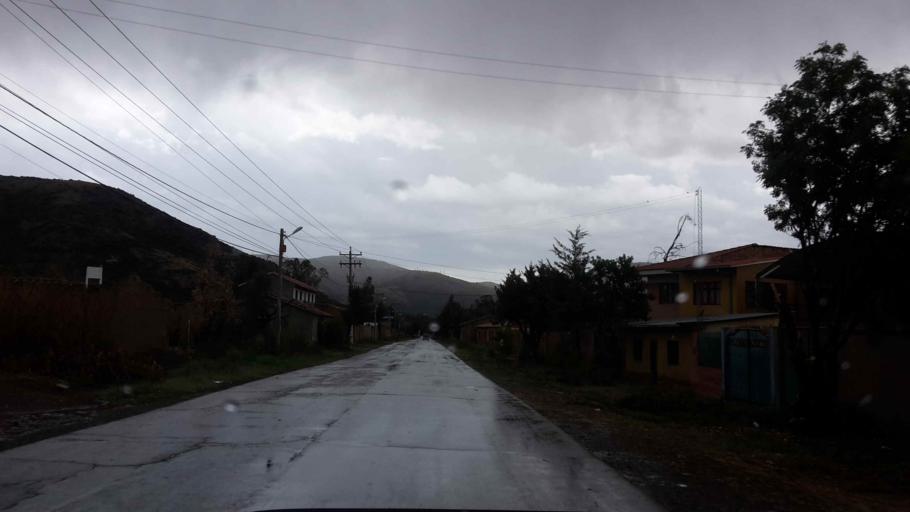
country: BO
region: Cochabamba
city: Tarata
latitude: -17.5484
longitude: -66.0989
